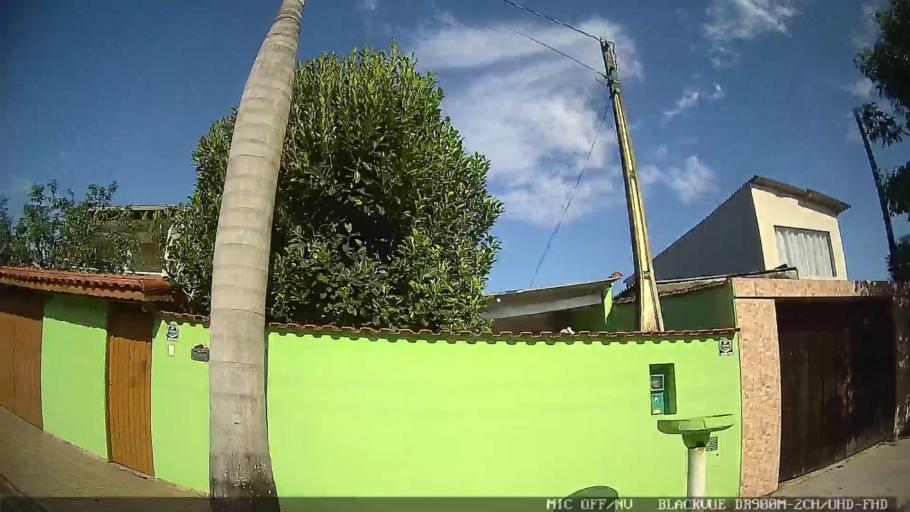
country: BR
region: Sao Paulo
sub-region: Itanhaem
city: Itanhaem
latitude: -24.1789
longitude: -46.8215
